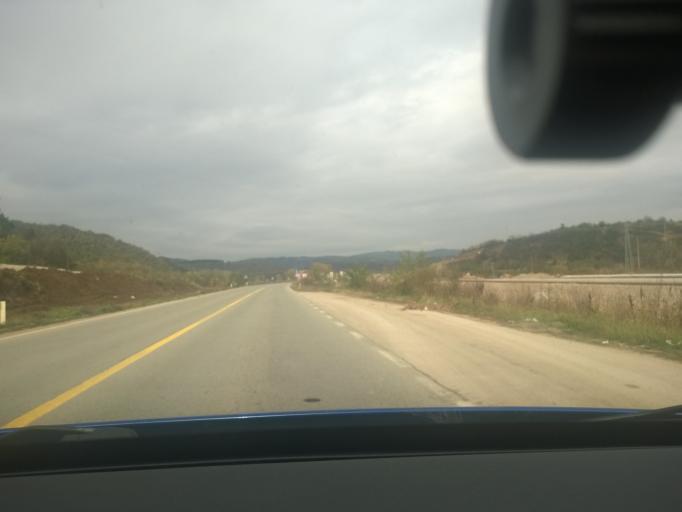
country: RS
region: Central Serbia
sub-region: Pirotski Okrug
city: Pirot
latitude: 43.2091
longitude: 22.5509
